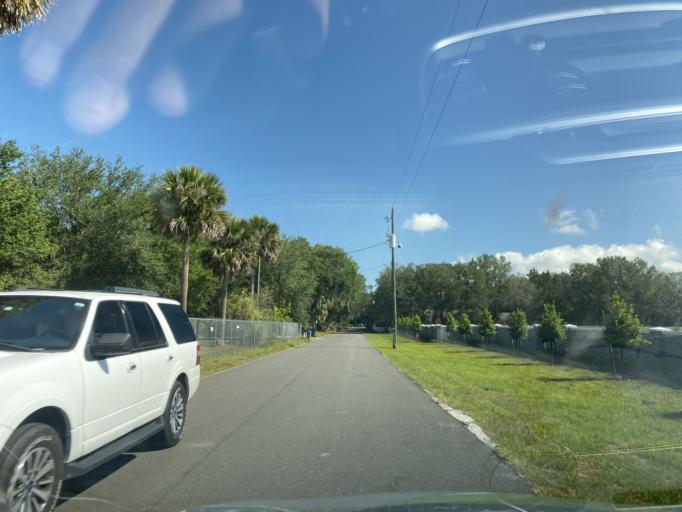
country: US
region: Florida
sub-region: Volusia County
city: DeBary
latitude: 28.8314
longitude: -81.3355
